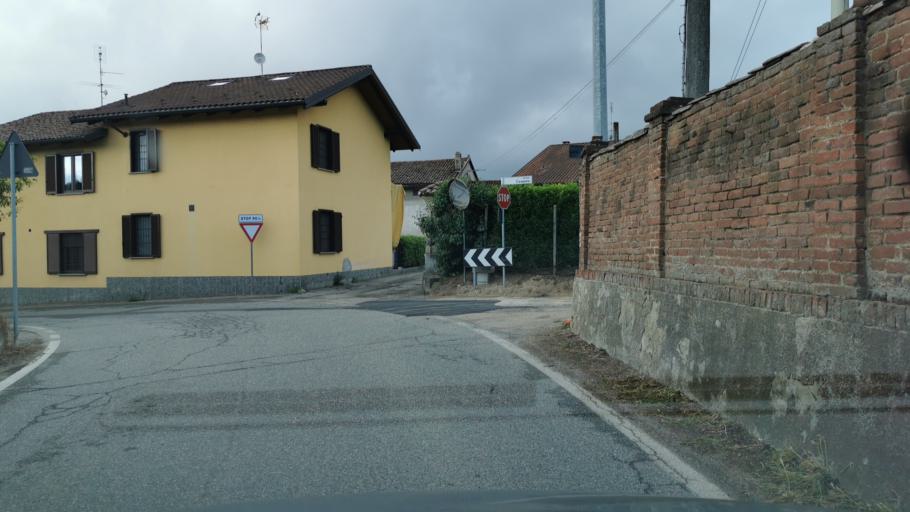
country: IT
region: Piedmont
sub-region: Provincia di Torino
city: Cambiano
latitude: 44.9987
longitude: 7.7833
